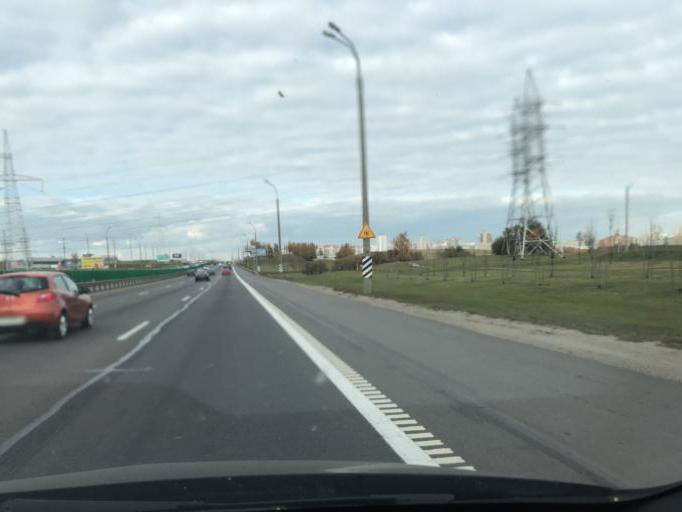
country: BY
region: Minsk
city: Malinovka
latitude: 53.8677
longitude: 27.4240
